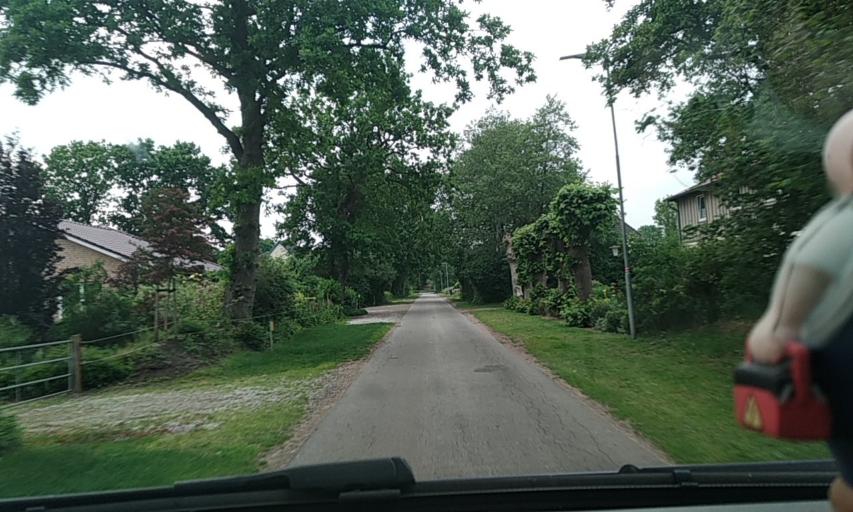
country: DE
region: Schleswig-Holstein
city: Borm
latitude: 54.3969
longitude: 9.3817
